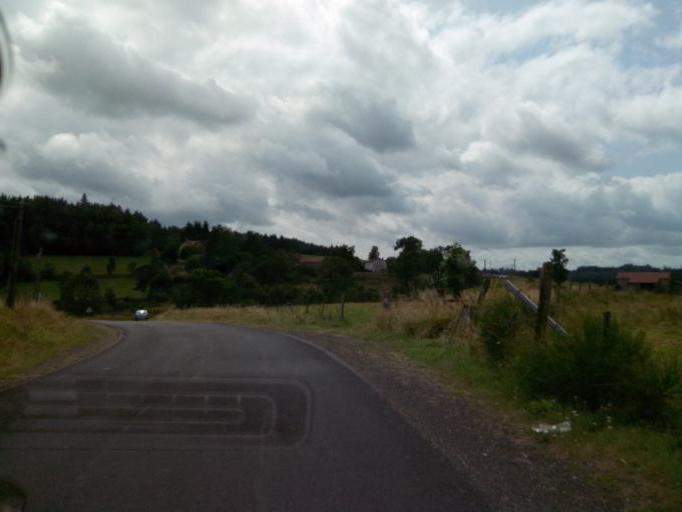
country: FR
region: Rhone-Alpes
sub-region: Departement de la Loire
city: Usson-en-Forez
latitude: 45.3850
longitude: 3.9429
